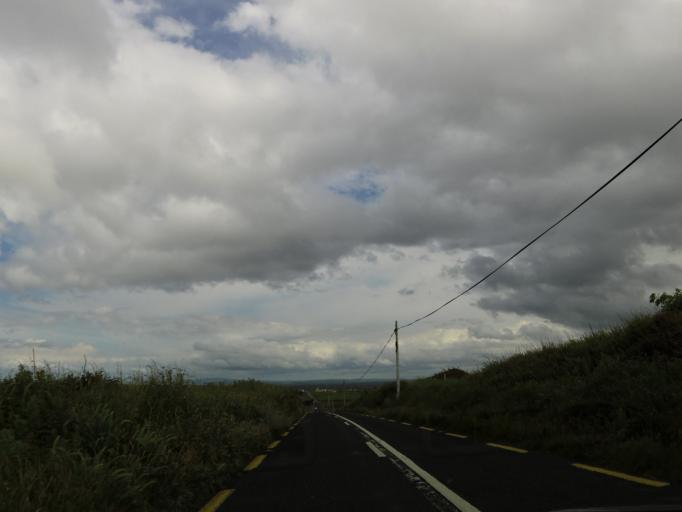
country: IE
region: Munster
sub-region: An Clar
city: Kilrush
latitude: 52.7023
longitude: -9.6189
